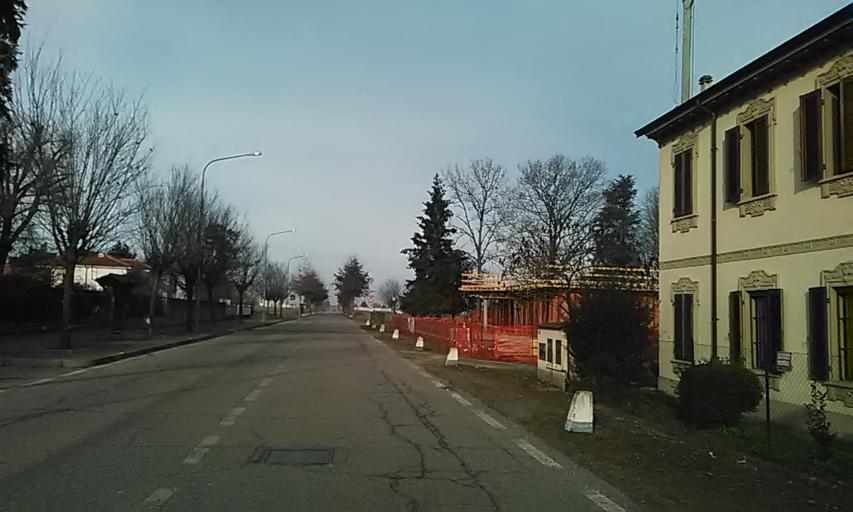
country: IT
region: Piedmont
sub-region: Provincia di Vercelli
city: Stroppiana
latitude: 45.2357
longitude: 8.4561
